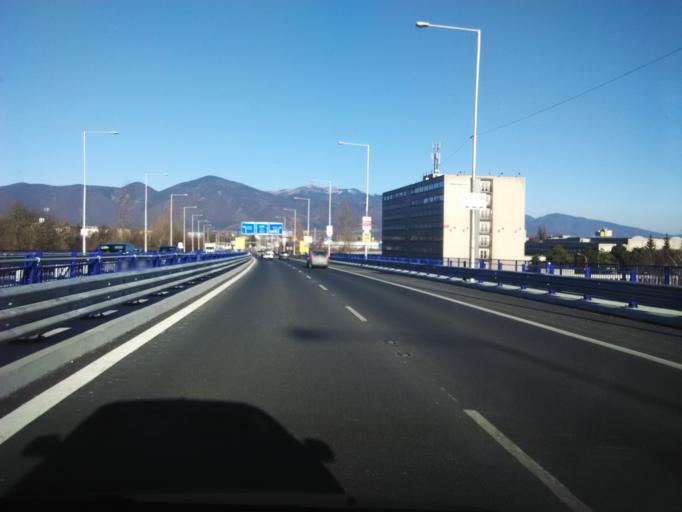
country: SK
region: Zilinsky
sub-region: Okres Martin
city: Martin
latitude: 49.0721
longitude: 18.9151
